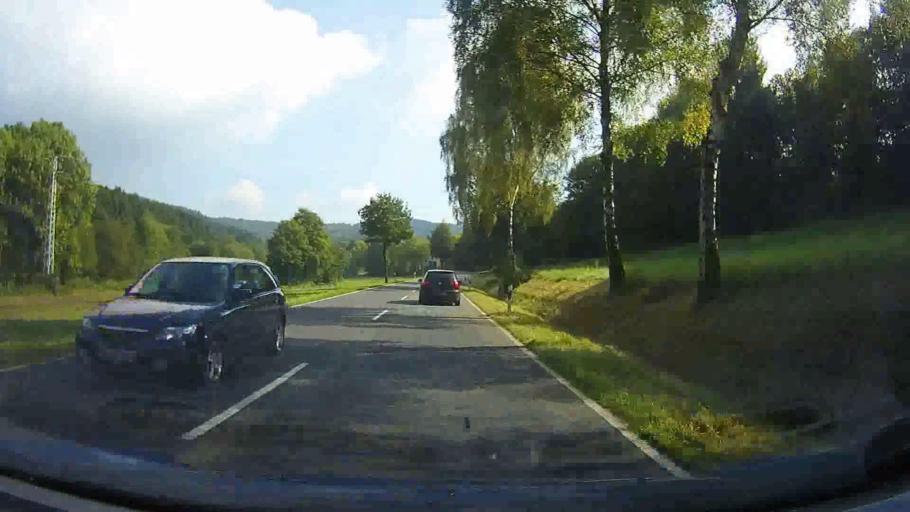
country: DE
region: Lower Saxony
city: Adelebsen
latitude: 51.6609
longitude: 9.7526
